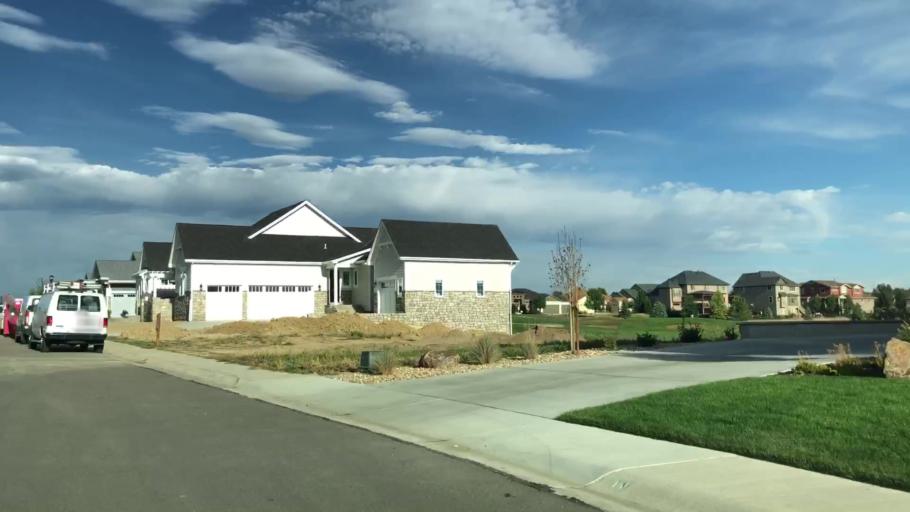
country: US
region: Colorado
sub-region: Weld County
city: Windsor
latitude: 40.4591
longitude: -104.9694
